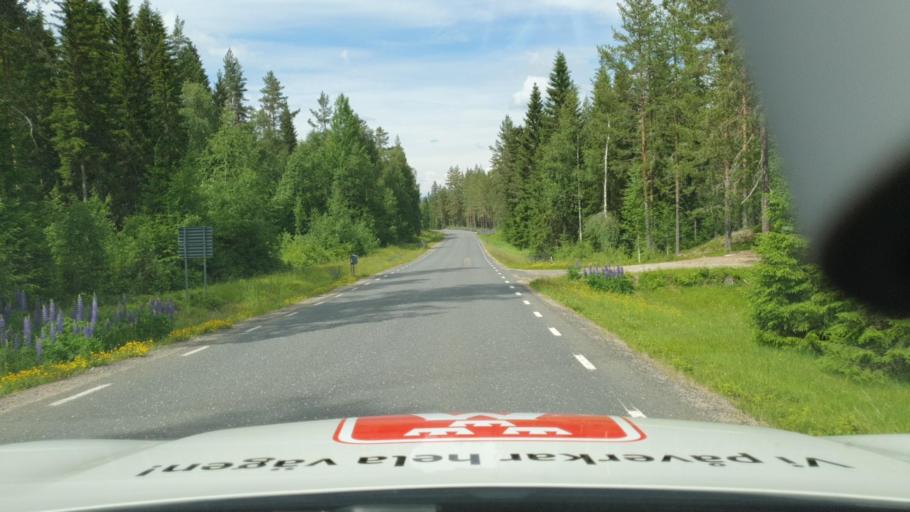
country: SE
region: Vaermland
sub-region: Torsby Kommun
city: Torsby
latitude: 60.6651
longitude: 12.6997
